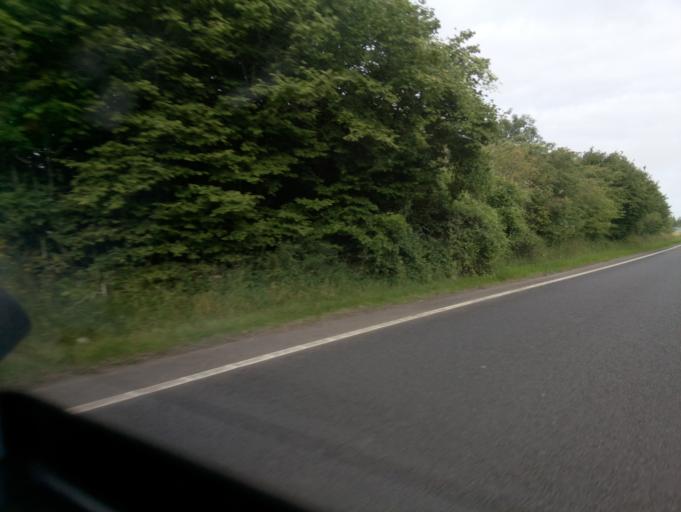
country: GB
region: England
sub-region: Gloucestershire
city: Coates
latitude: 51.7783
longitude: -2.0317
